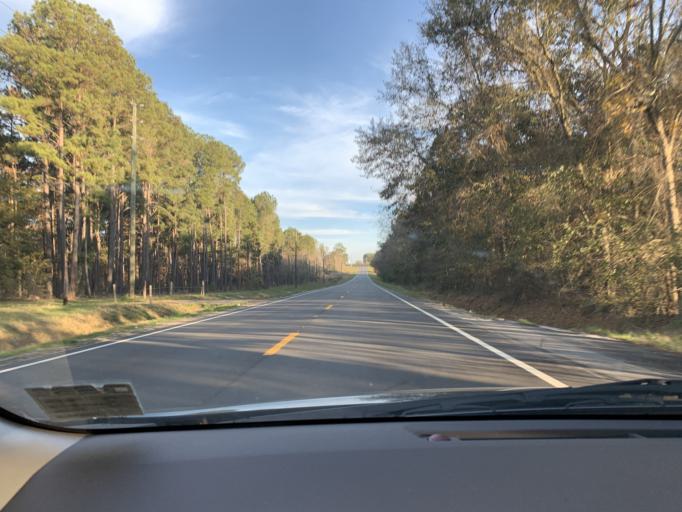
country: US
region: Georgia
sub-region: Coffee County
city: Broxton
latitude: 31.5808
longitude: -83.0626
